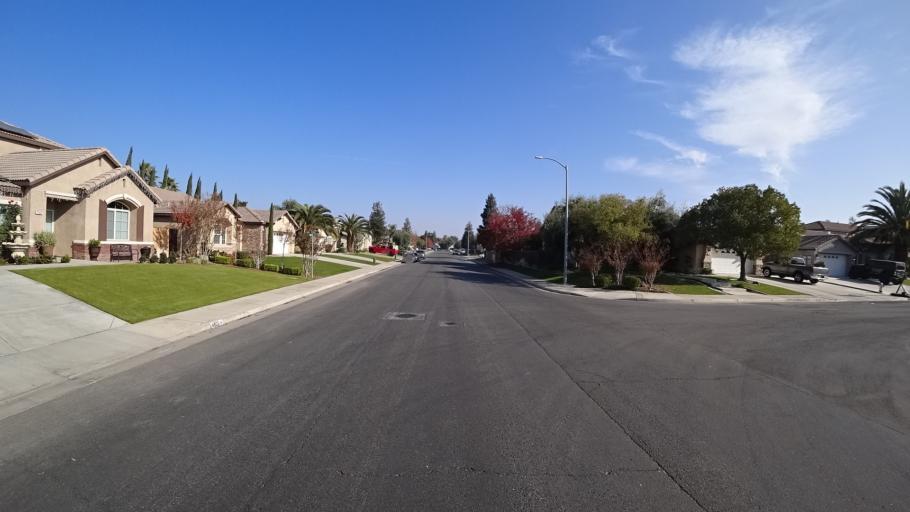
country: US
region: California
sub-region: Kern County
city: Rosedale
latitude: 35.3603
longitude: -119.1684
